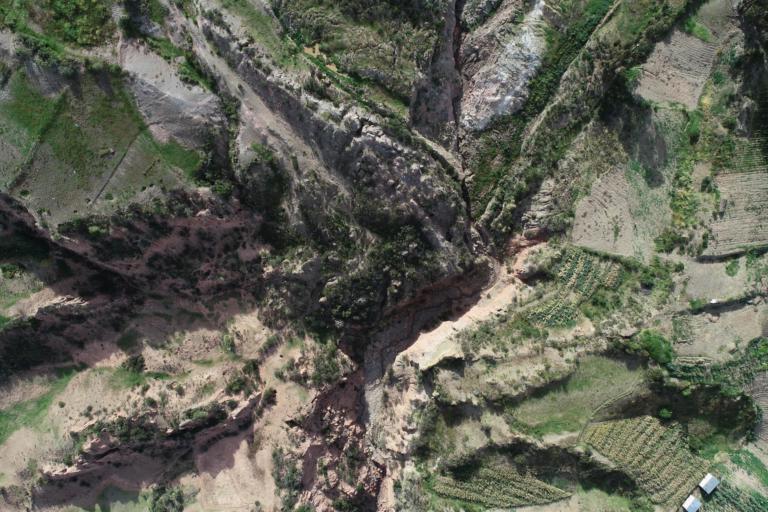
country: BO
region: La Paz
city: La Paz
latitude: -16.5517
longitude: -67.9938
